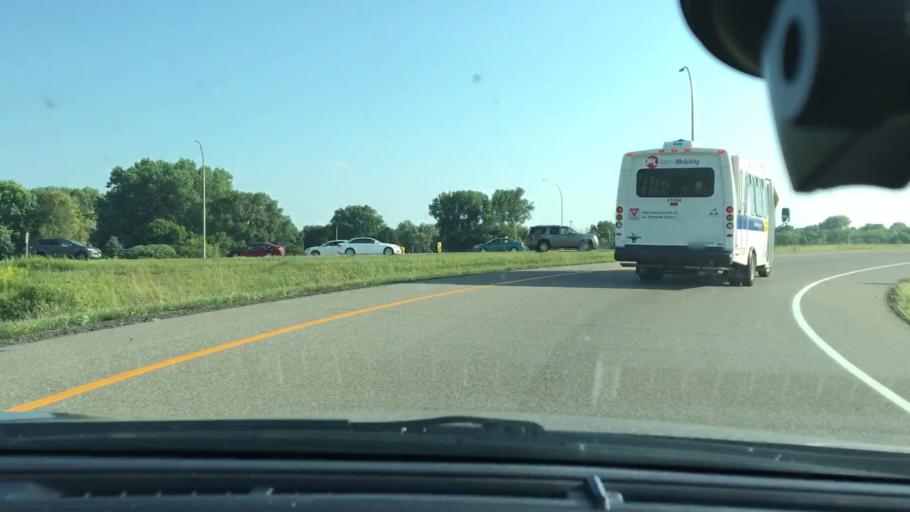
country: US
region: Minnesota
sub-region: Hennepin County
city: New Hope
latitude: 45.0343
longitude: -93.3992
